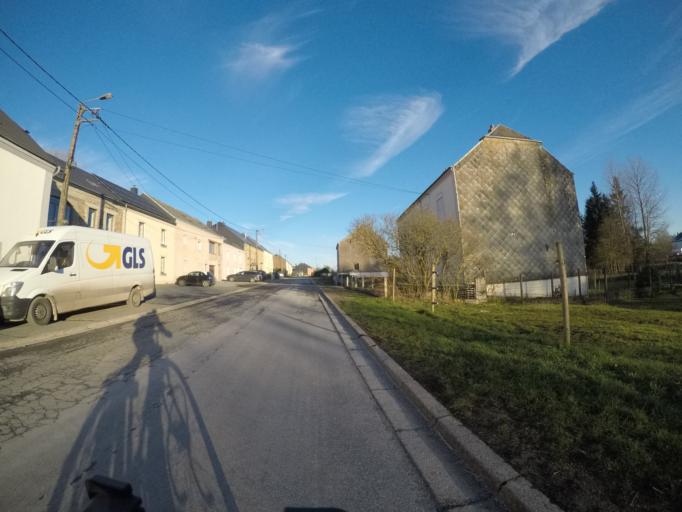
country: BE
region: Wallonia
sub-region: Province du Luxembourg
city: Habay-la-Vieille
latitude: 49.7204
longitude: 5.5852
